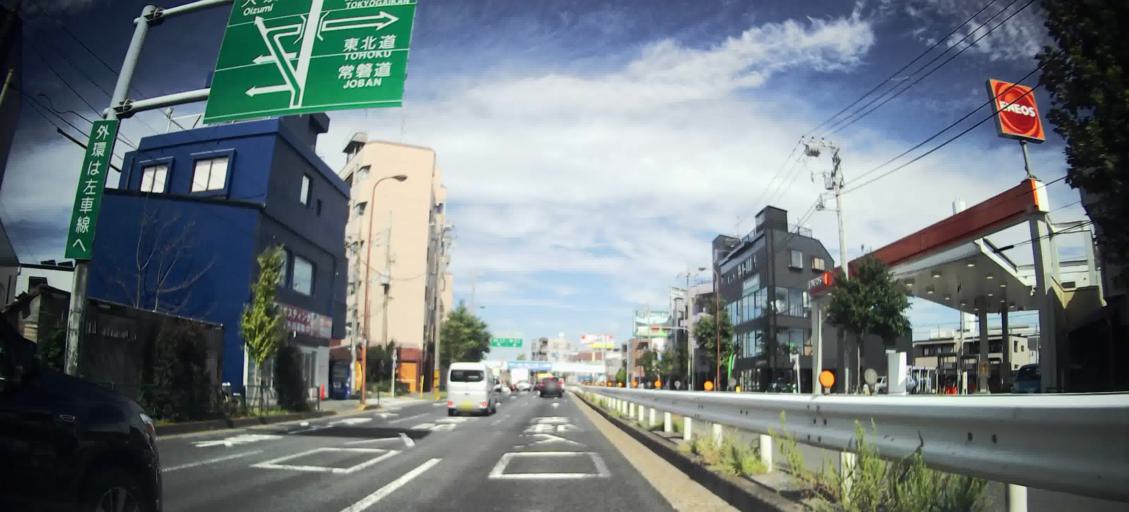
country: JP
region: Saitama
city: Wako
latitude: 35.7534
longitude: 139.6088
